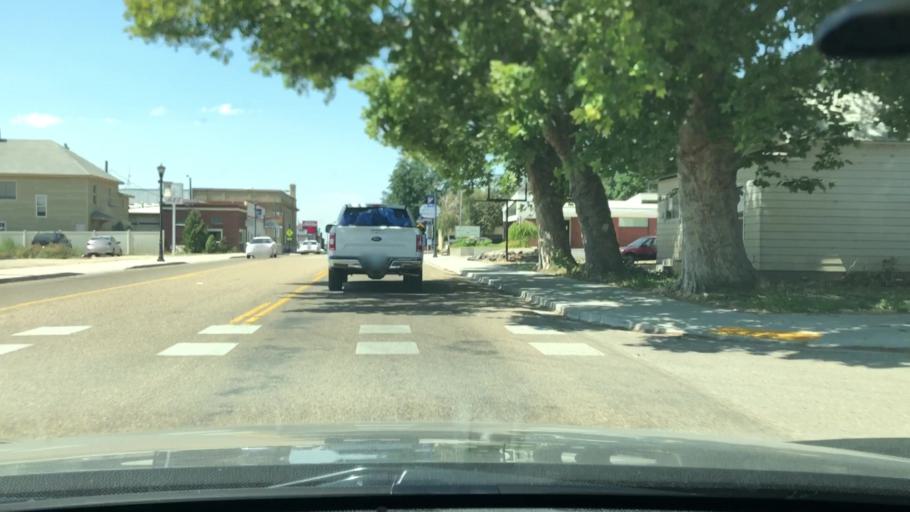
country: US
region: Idaho
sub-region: Canyon County
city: Parma
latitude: 43.7850
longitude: -116.9429
